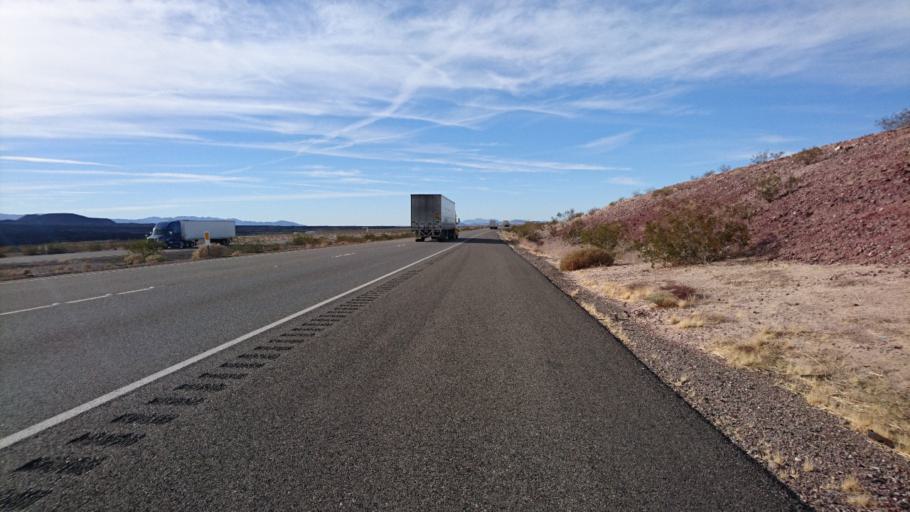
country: US
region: California
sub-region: San Bernardino County
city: Joshua Tree
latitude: 34.7502
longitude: -116.3341
